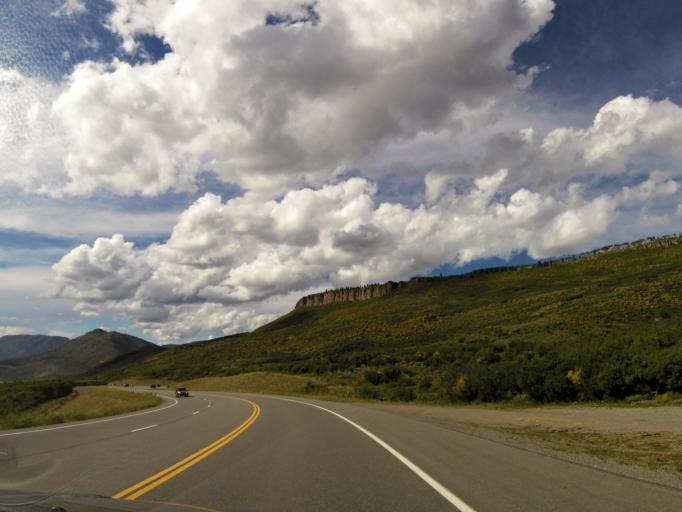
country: US
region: Colorado
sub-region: Hinsdale County
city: Lake City
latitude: 38.3929
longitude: -107.4448
